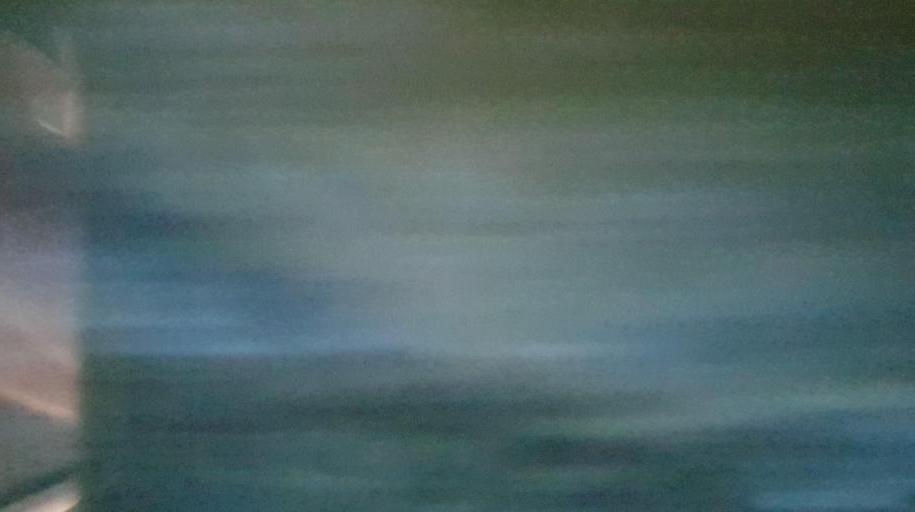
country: NO
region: Buskerud
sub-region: Drammen
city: Skoger
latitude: 59.7004
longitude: 10.2410
